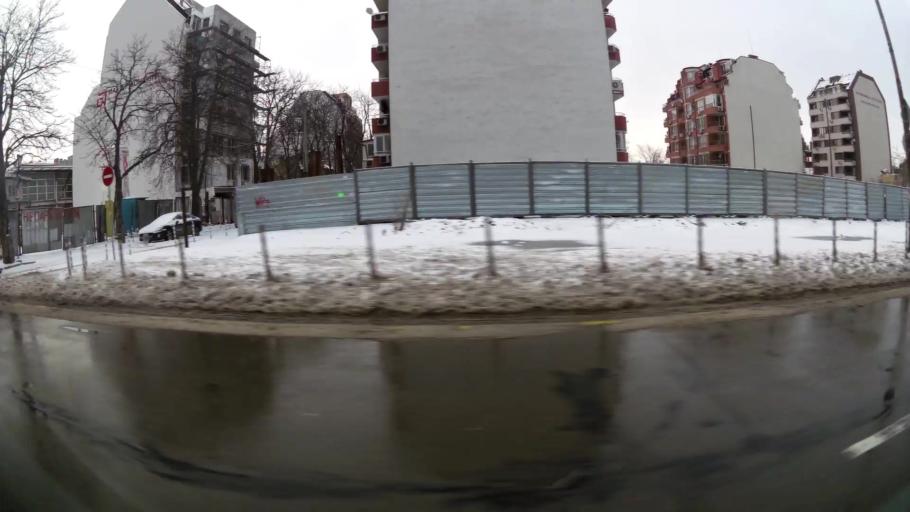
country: BG
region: Sofia-Capital
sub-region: Stolichna Obshtina
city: Sofia
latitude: 42.7014
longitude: 23.3018
